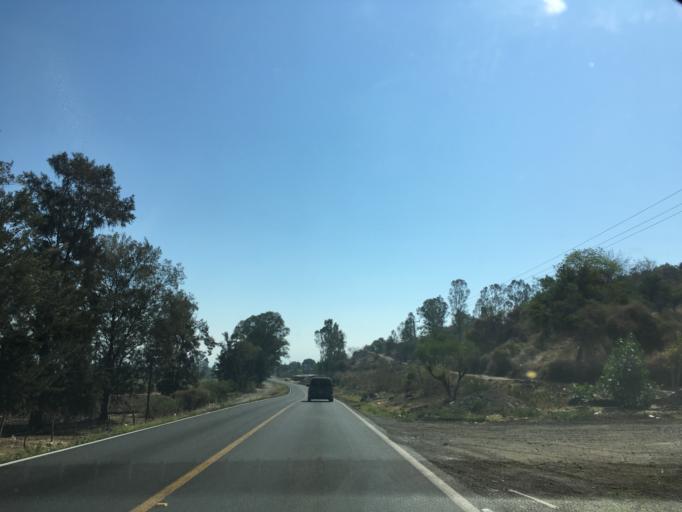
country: MX
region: Michoacan
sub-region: Indaparapeo
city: San Lucas Pio
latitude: 19.7958
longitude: -100.9212
